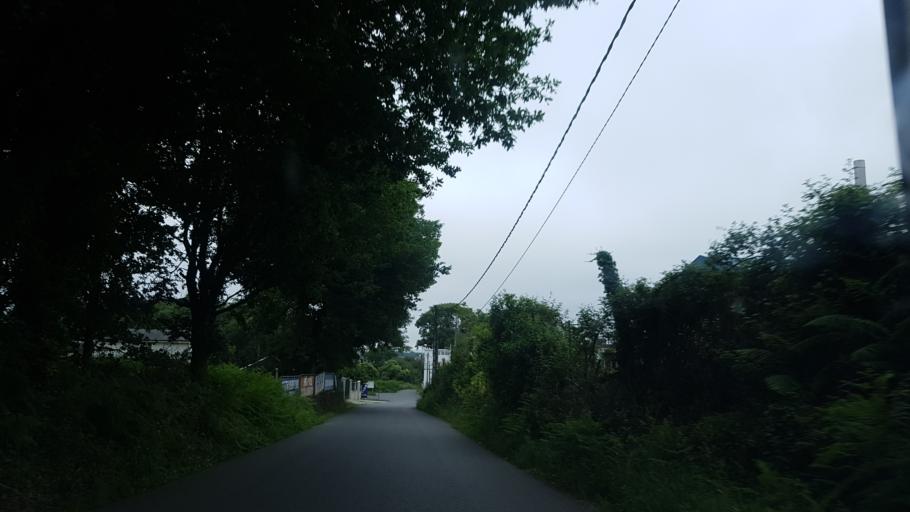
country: ES
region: Galicia
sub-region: Provincia de Lugo
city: Lugo
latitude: 43.0449
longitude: -7.5808
